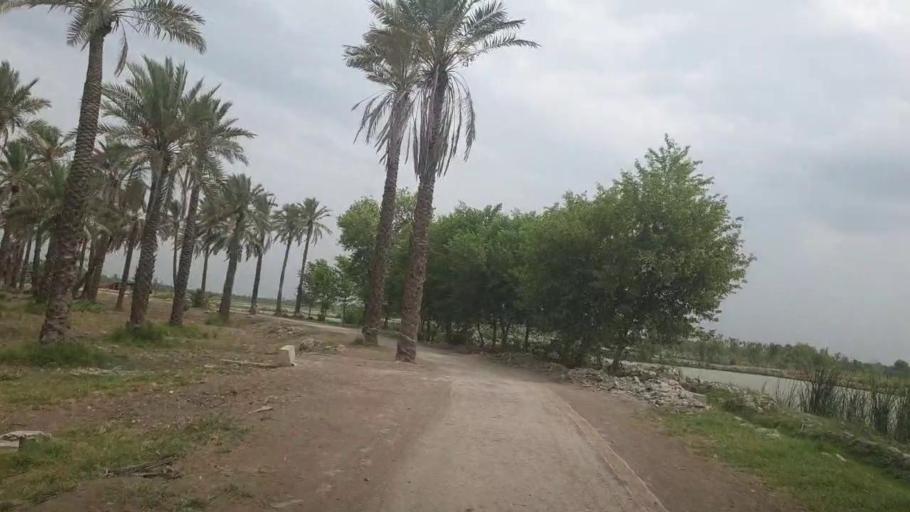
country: PK
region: Sindh
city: Khairpur
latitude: 27.5826
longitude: 68.7402
